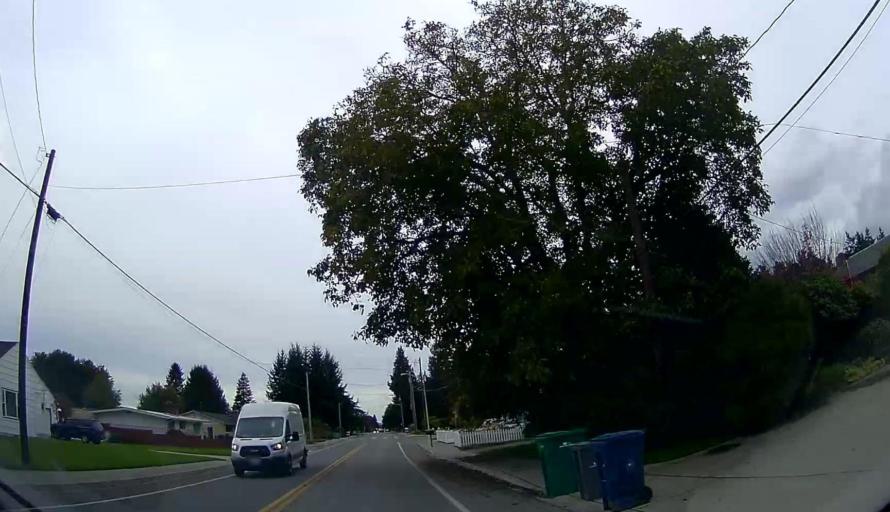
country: US
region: Washington
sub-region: Skagit County
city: Burlington
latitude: 48.4716
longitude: -122.3111
